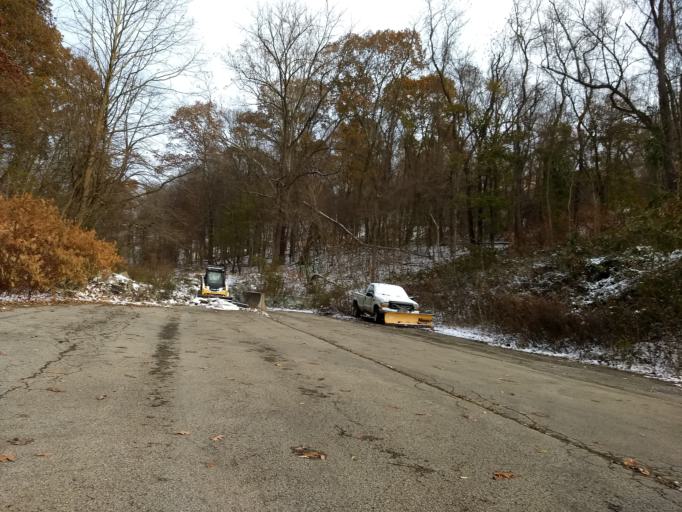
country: US
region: Pennsylvania
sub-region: Allegheny County
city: Mount Oliver
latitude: 40.4022
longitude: -79.9992
